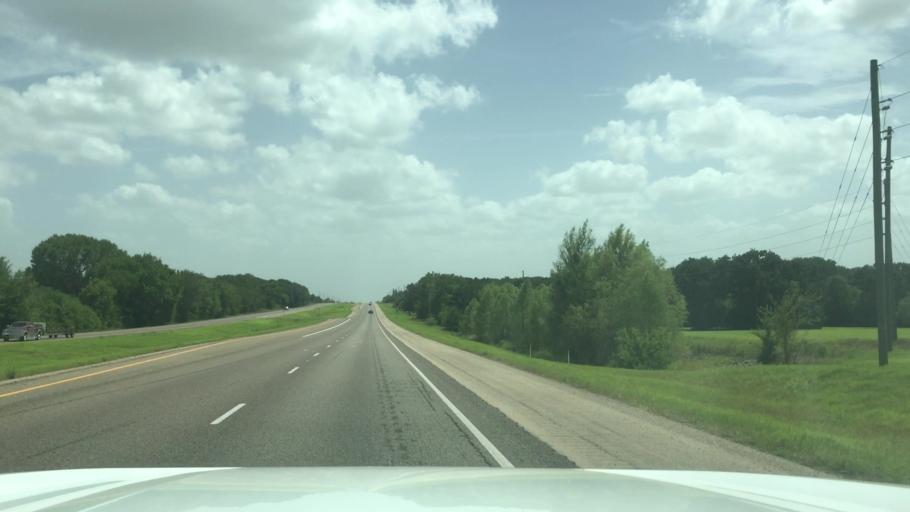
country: US
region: Texas
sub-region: Robertson County
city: Calvert
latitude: 31.0902
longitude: -96.7145
